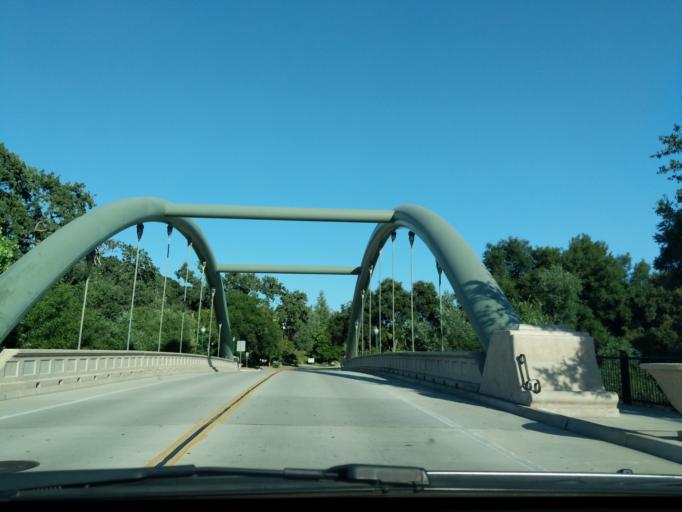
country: US
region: California
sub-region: San Luis Obispo County
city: Atascadero
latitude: 35.4898
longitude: -120.6659
